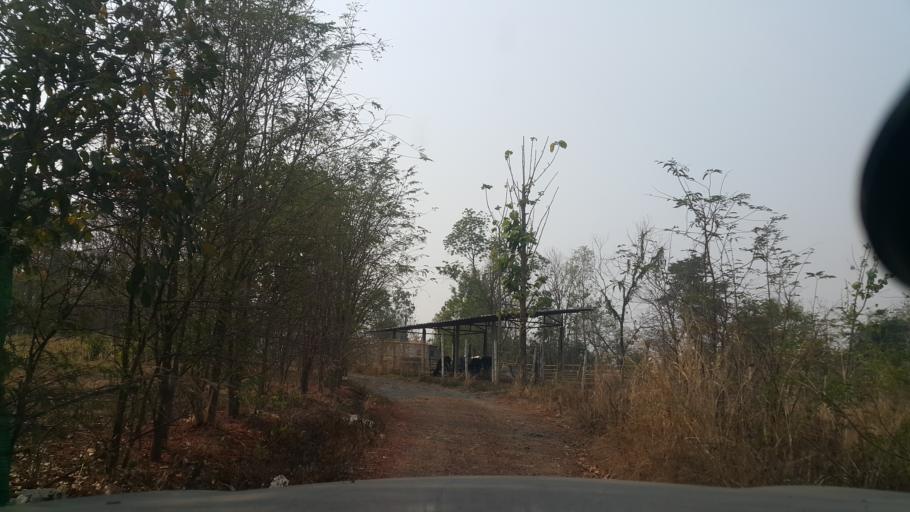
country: TH
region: Chiang Mai
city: Mae On
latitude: 18.7752
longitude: 99.2692
